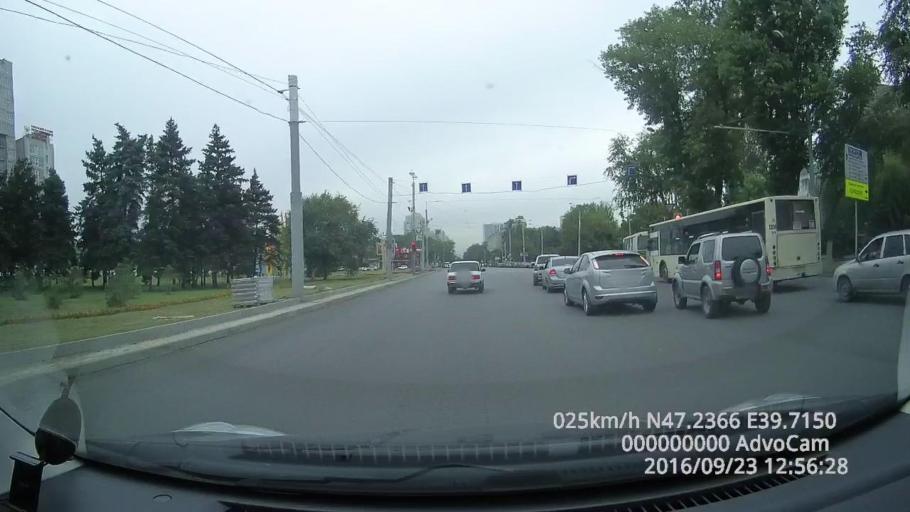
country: RU
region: Rostov
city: Rostov-na-Donu
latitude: 47.2366
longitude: 39.7149
